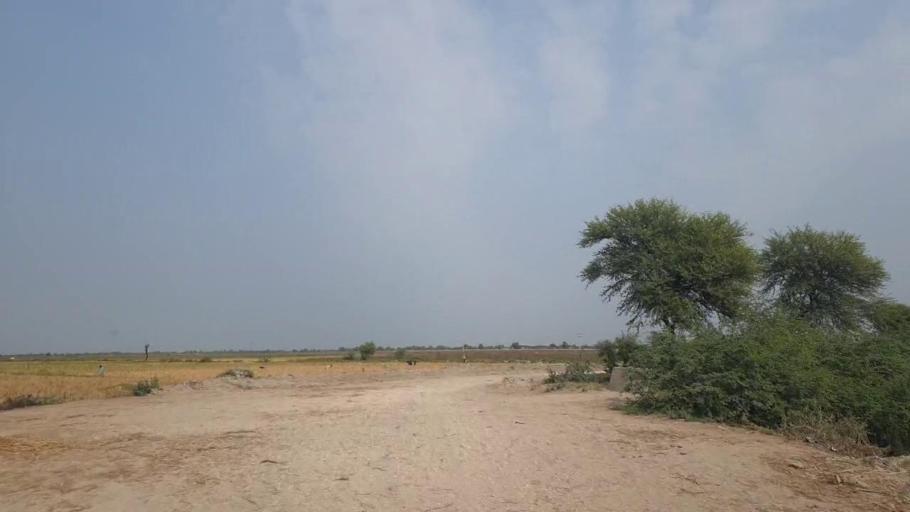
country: PK
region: Sindh
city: Badin
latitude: 24.6186
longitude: 68.7413
